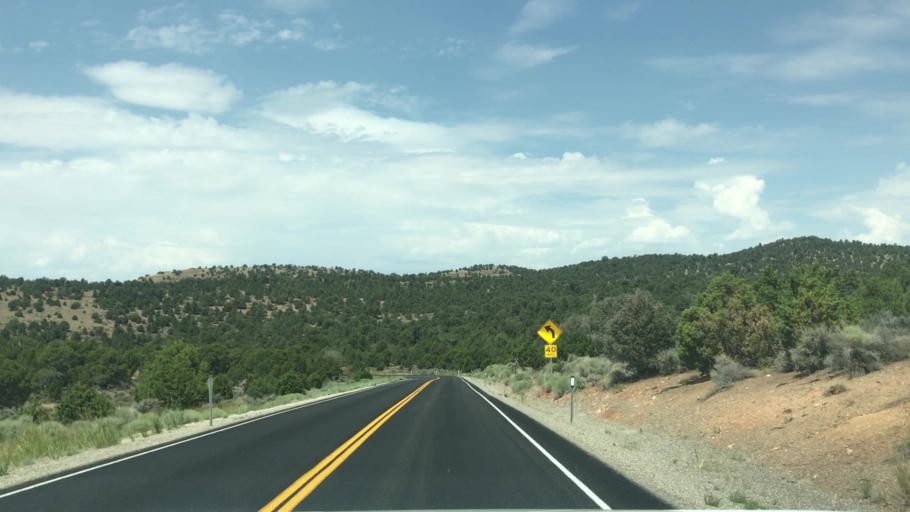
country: US
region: Nevada
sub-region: Eureka County
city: Eureka
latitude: 39.3979
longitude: -115.4705
